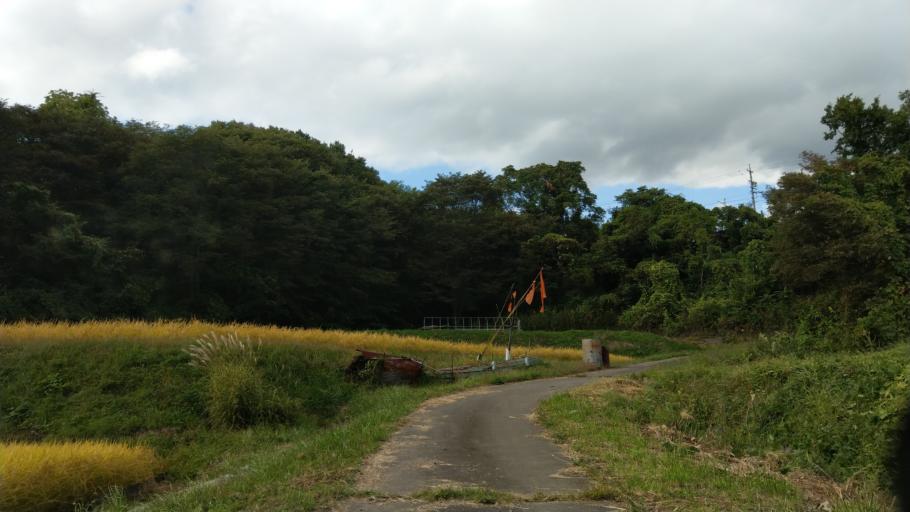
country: JP
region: Nagano
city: Komoro
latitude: 36.3483
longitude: 138.4228
